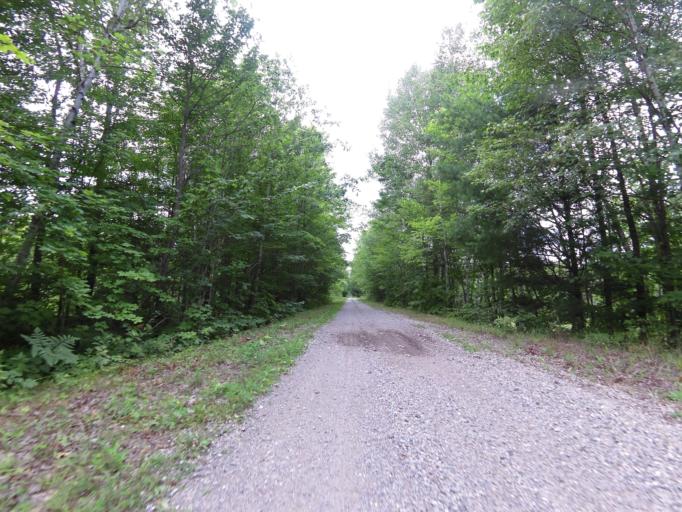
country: CA
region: Ontario
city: Perth
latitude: 44.8129
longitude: -76.6050
